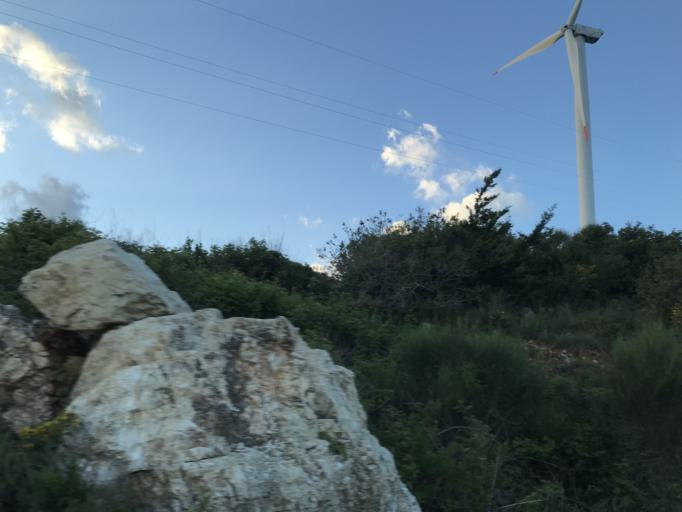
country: TR
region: Hatay
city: Buyukcat
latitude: 36.0968
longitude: 36.0394
